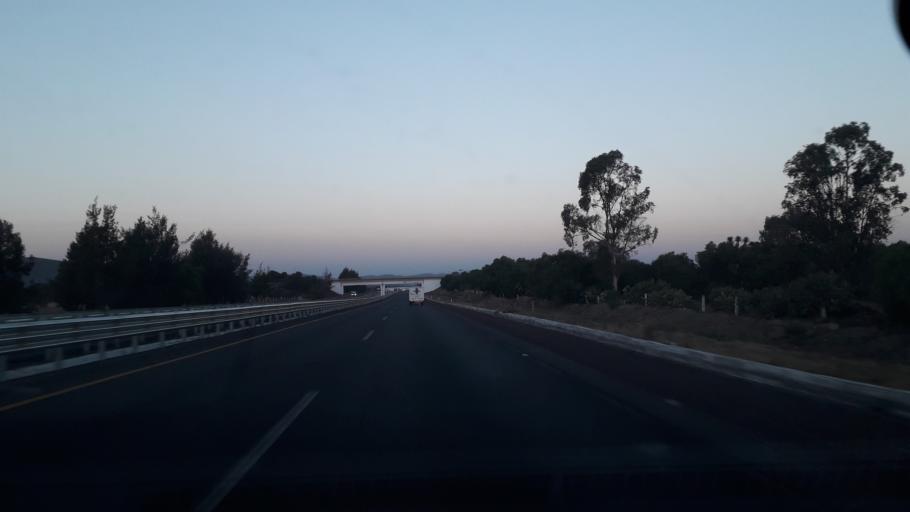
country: MX
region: Puebla
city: San Jose Esperanza
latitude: 18.8526
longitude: -97.4221
